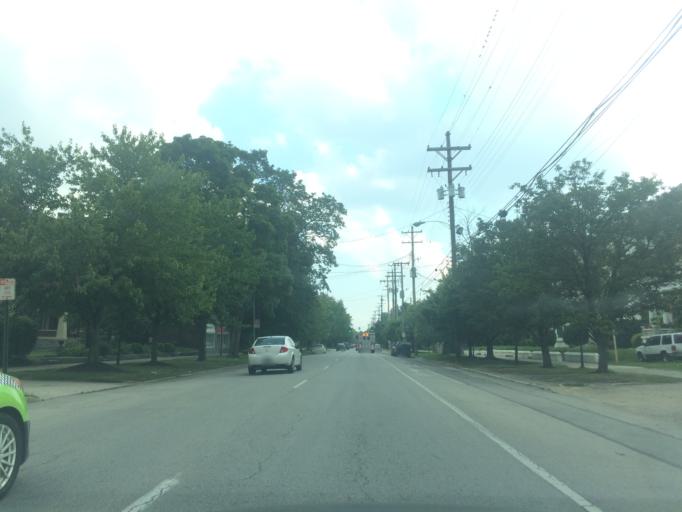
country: US
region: Kentucky
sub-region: Jefferson County
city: Louisville
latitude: 38.2388
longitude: -85.7580
